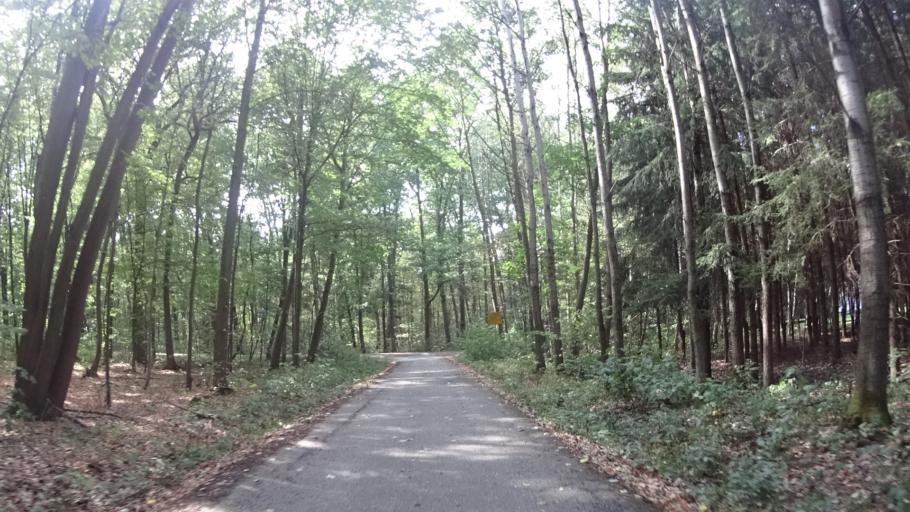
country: CZ
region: Olomoucky
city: Naklo
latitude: 49.6860
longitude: 17.1235
